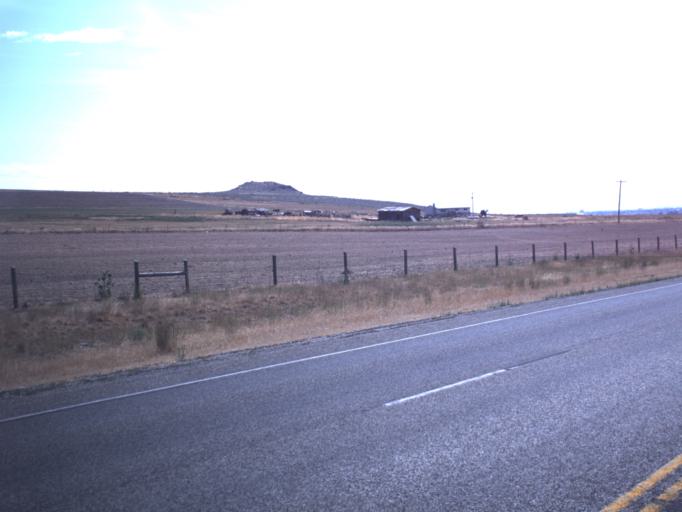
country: US
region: Utah
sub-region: Box Elder County
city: Garland
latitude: 41.7871
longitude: -112.0838
